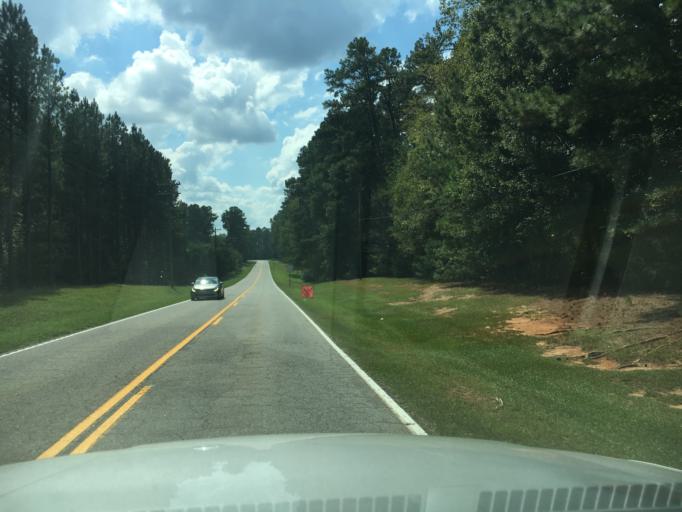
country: US
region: South Carolina
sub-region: Greenwood County
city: Greenwood
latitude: 34.1146
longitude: -82.1270
